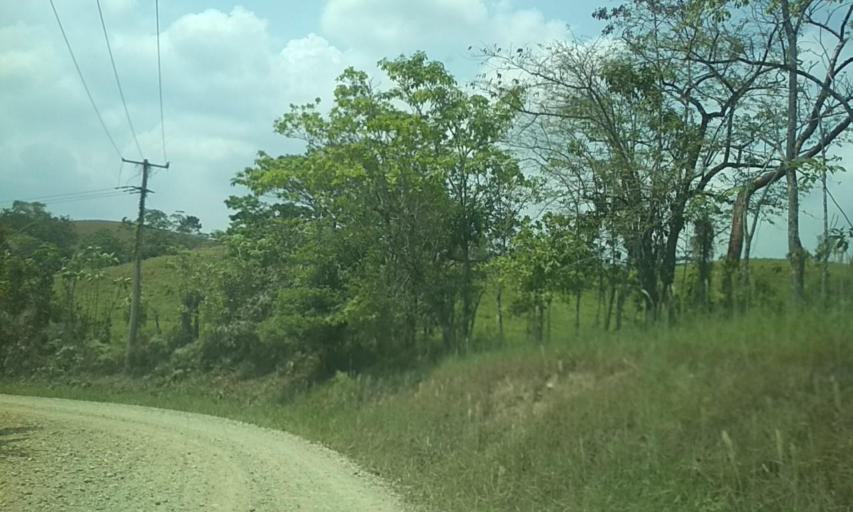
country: MX
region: Tabasco
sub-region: Huimanguillo
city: Francisco Rueda
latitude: 17.6194
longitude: -93.8144
